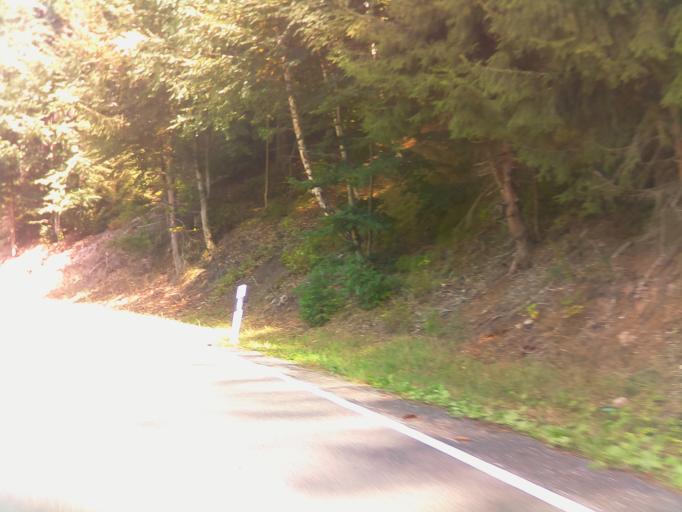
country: DE
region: Thuringia
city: Schwarza
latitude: 50.6319
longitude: 10.5314
